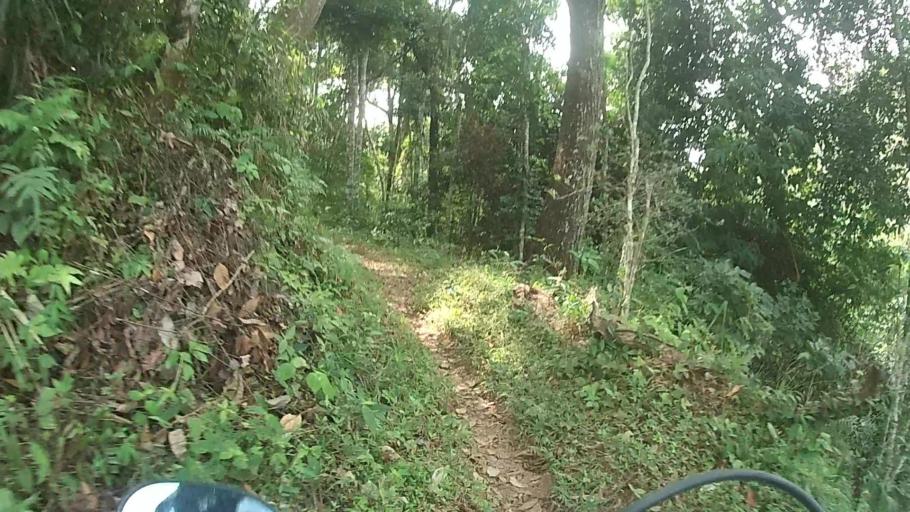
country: TH
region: Lampang
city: Mueang Pan
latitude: 18.7972
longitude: 99.3808
